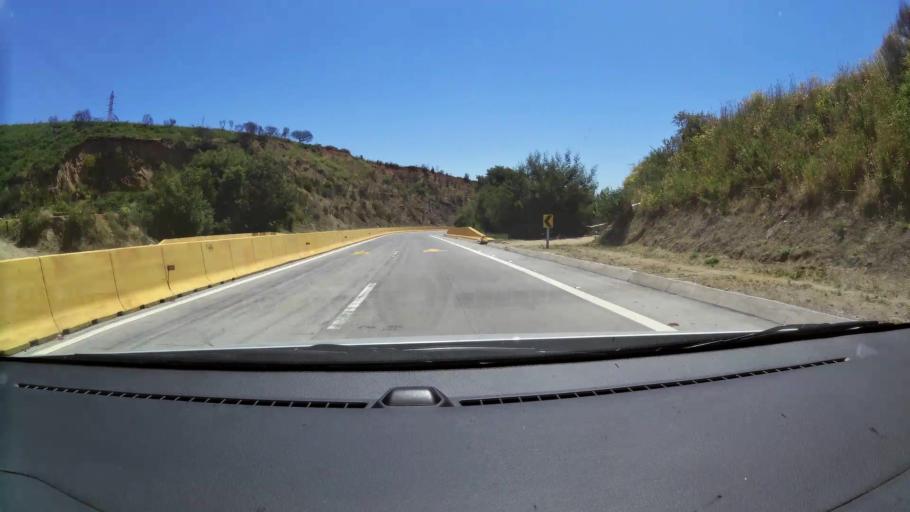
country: CL
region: Valparaiso
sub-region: Provincia de Valparaiso
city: Valparaiso
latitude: -33.0606
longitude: -71.6440
